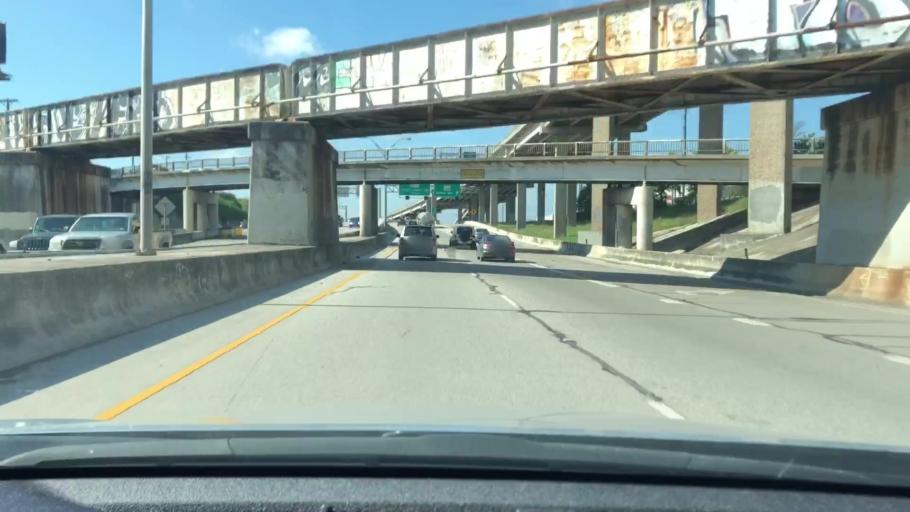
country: US
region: Texas
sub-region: Bexar County
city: Windcrest
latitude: 29.5208
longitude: -98.3961
